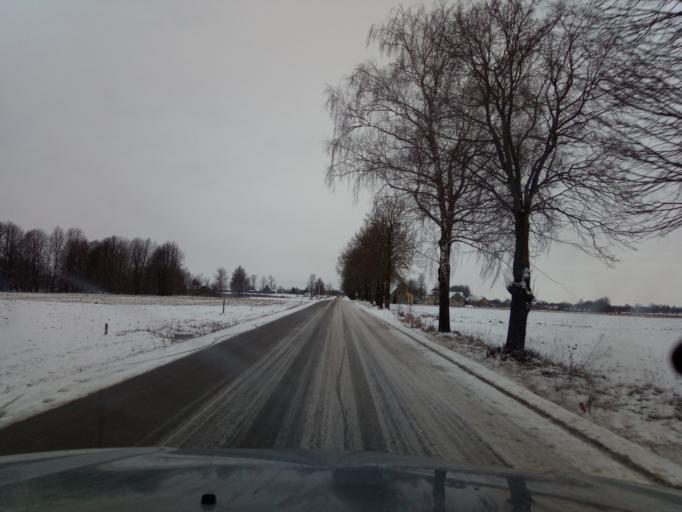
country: LT
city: Ramygala
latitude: 55.4924
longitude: 24.4968
